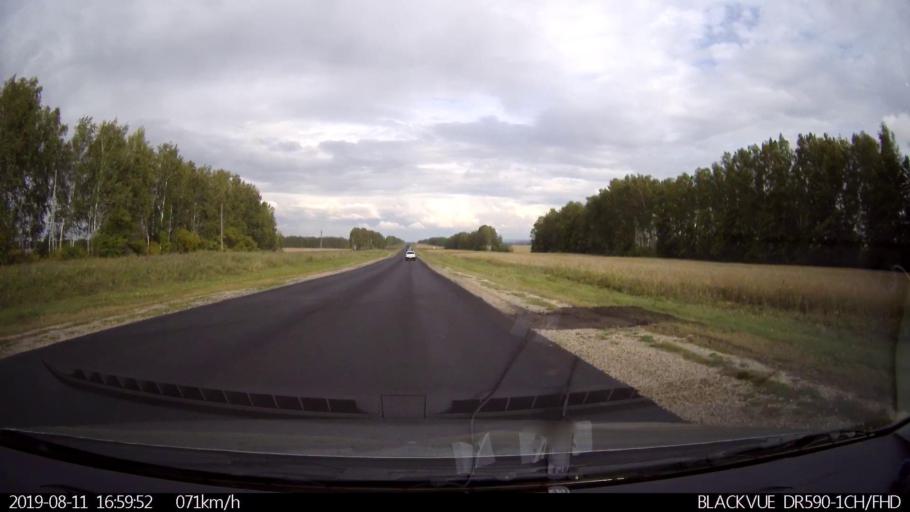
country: RU
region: Ulyanovsk
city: Mayna
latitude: 54.3116
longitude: 47.6691
